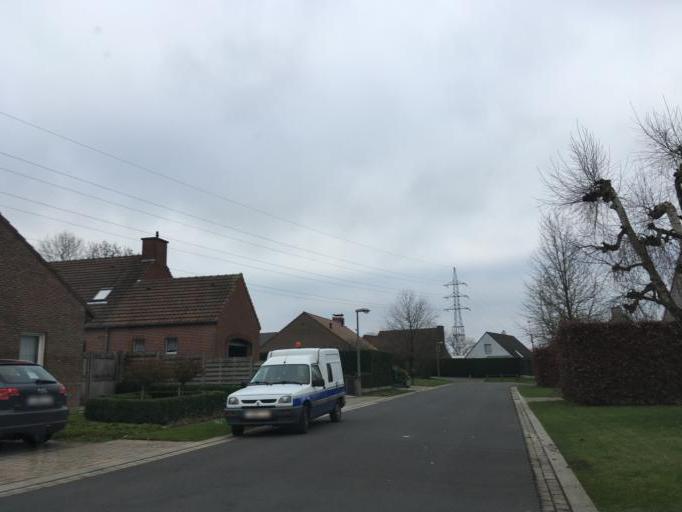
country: BE
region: Flanders
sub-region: Provincie West-Vlaanderen
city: Roeselare
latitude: 50.9576
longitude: 3.1391
